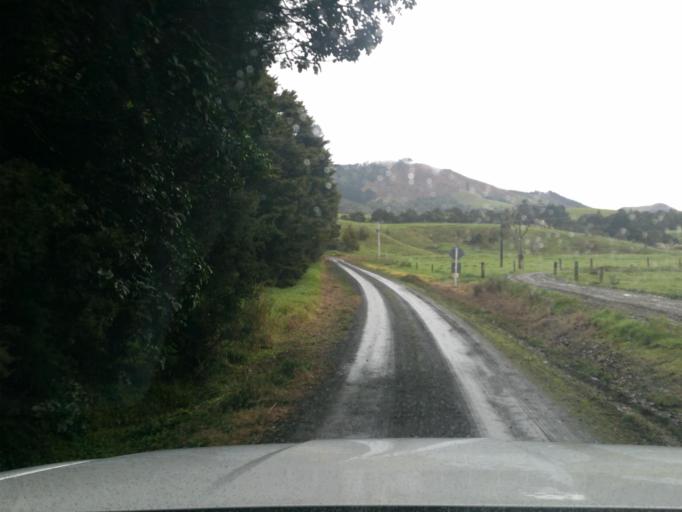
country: NZ
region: Northland
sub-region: Kaipara District
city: Dargaville
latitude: -35.8091
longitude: 173.8558
